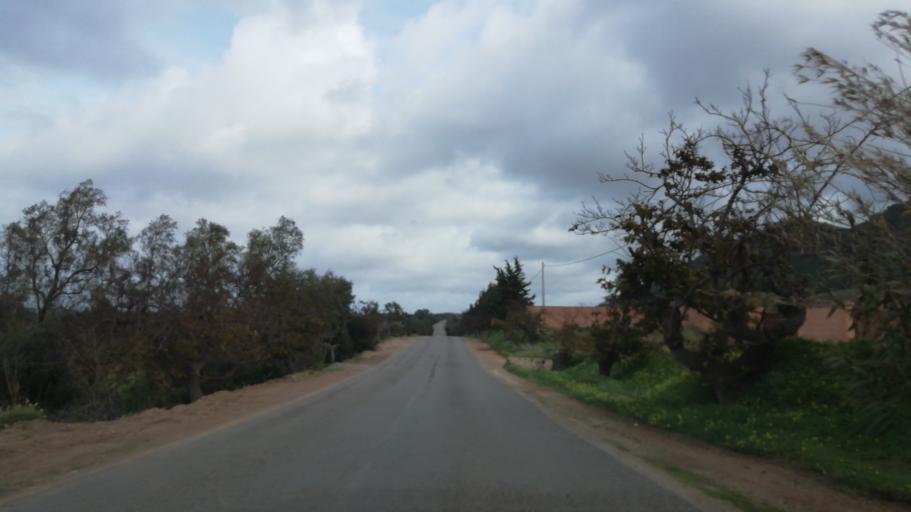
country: DZ
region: Oran
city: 'Ain el Turk
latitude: 35.7002
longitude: -0.8472
